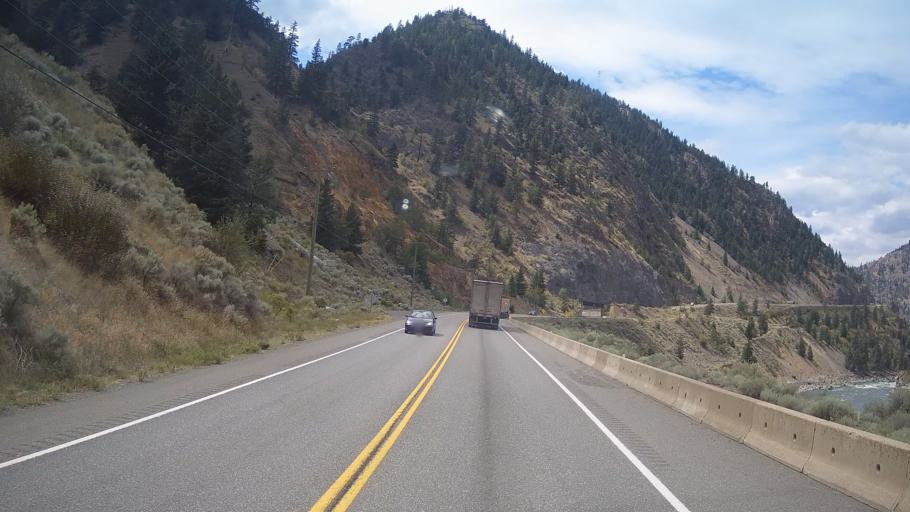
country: CA
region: British Columbia
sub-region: Thompson-Nicola Regional District
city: Ashcroft
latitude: 50.2556
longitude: -121.4389
